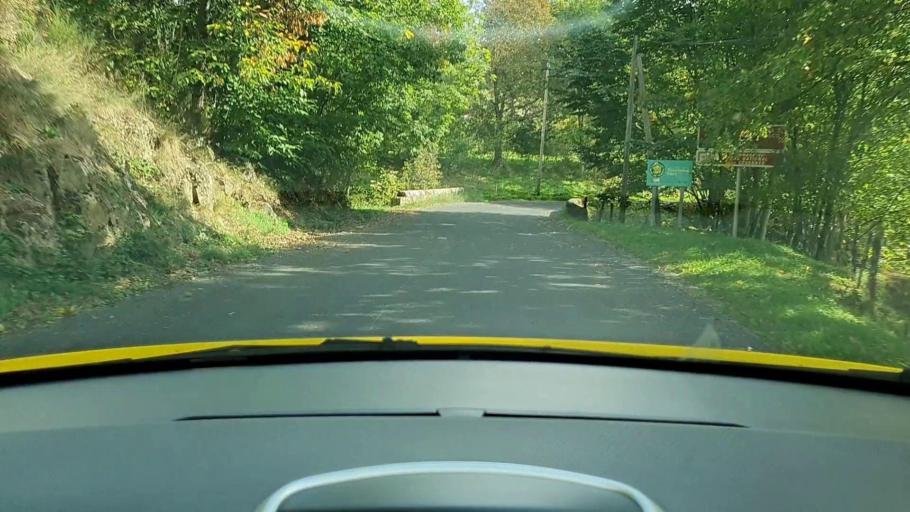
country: FR
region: Languedoc-Roussillon
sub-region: Departement de la Lozere
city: Meyrueis
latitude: 44.0670
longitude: 3.4411
